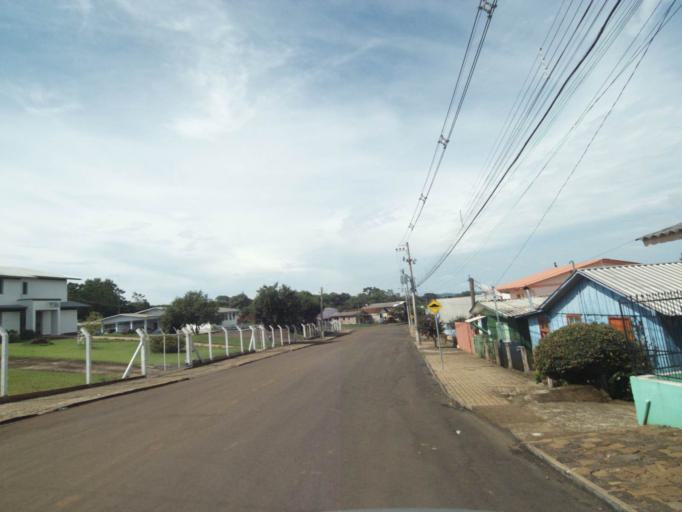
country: BR
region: Rio Grande do Sul
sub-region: Lagoa Vermelha
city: Lagoa Vermelha
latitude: -28.2213
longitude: -51.5153
